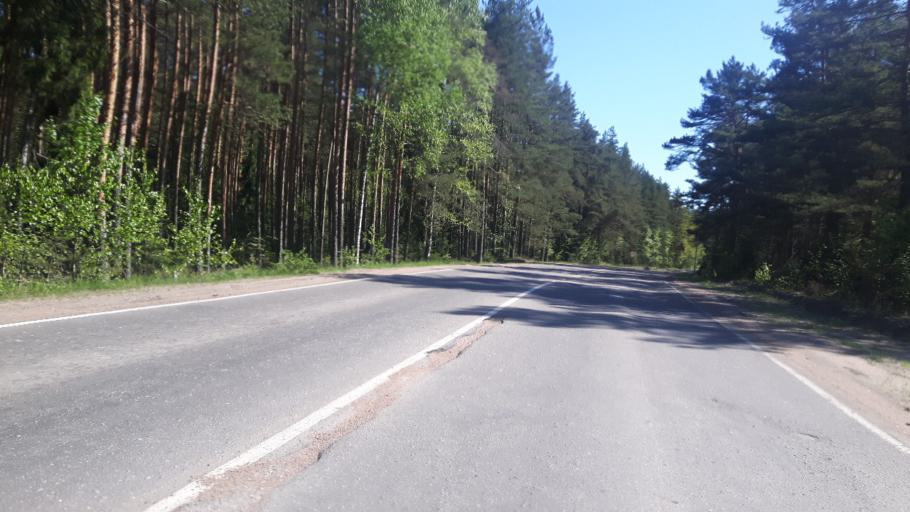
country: RU
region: Leningrad
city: Glebychevo
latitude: 60.2402
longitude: 29.0026
